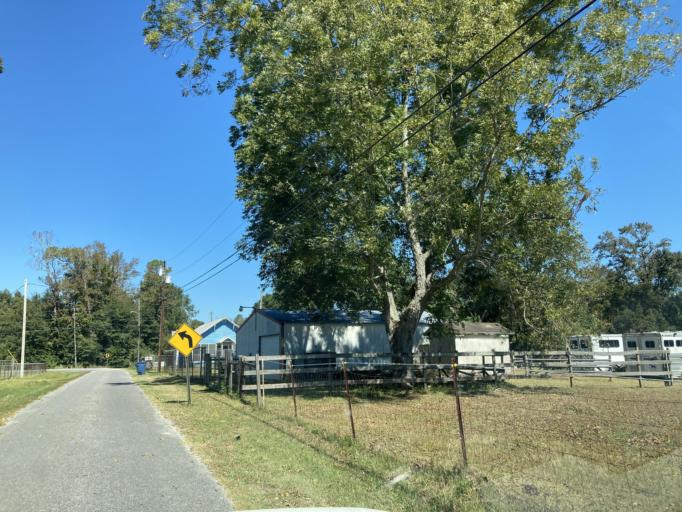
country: US
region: Mississippi
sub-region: Jackson County
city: Saint Martin
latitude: 30.4712
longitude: -88.8750
